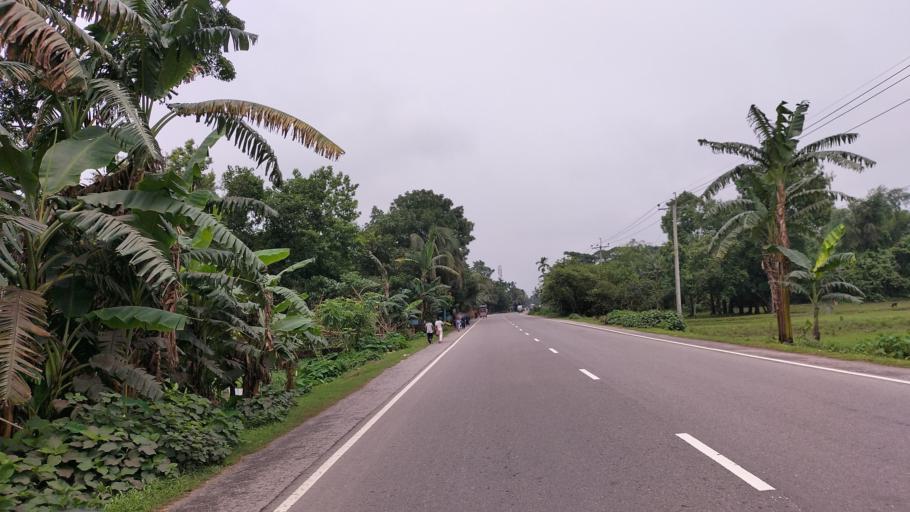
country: BD
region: Dhaka
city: Netrakona
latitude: 24.8503
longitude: 90.6373
